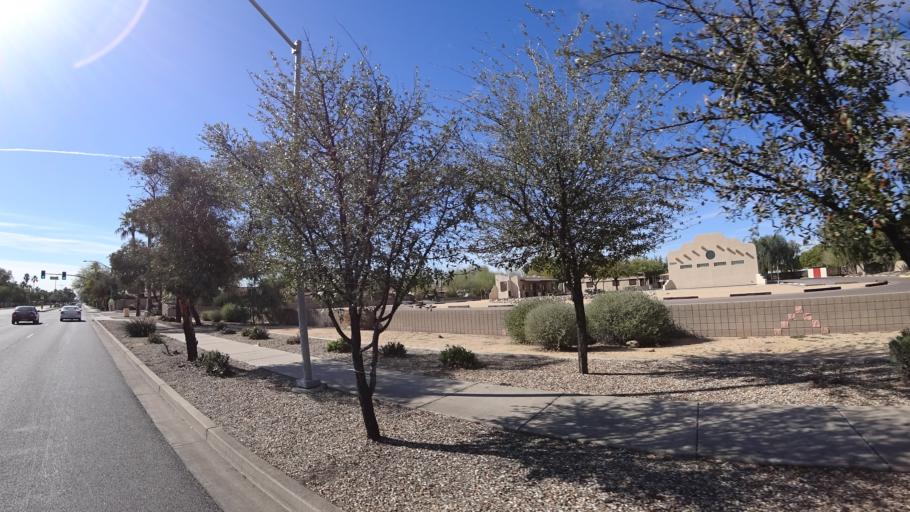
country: US
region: Arizona
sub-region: Maricopa County
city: Glendale
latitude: 33.5898
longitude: -112.1862
